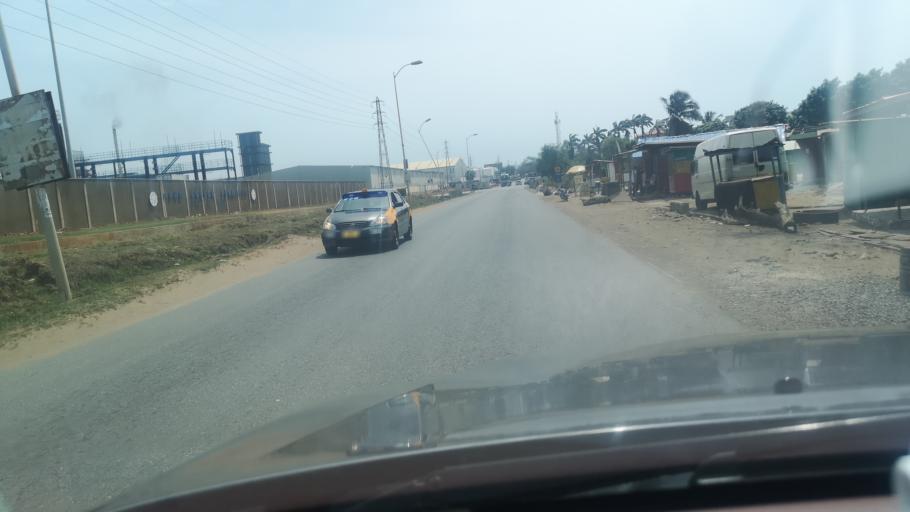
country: GH
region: Greater Accra
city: Tema
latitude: 5.6263
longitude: -0.0141
